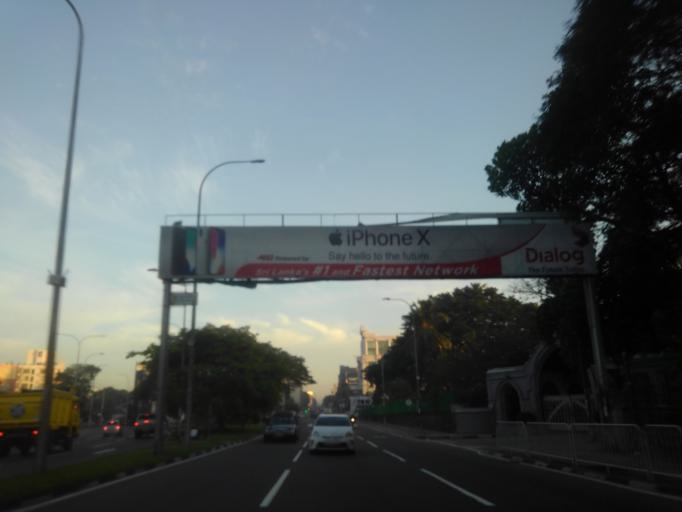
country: LK
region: Western
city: Kolonnawa
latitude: 6.9077
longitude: 79.8774
